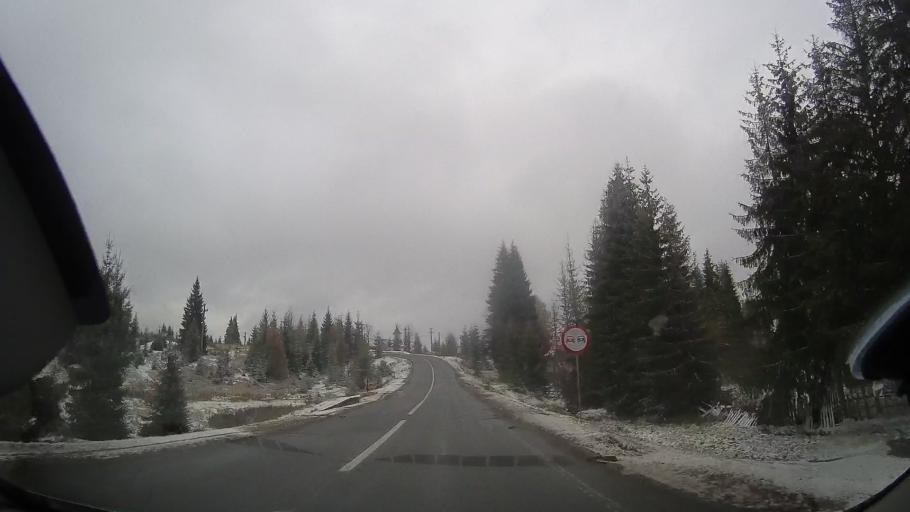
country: RO
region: Cluj
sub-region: Comuna Belis
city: Belis
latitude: 46.6909
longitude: 23.0383
